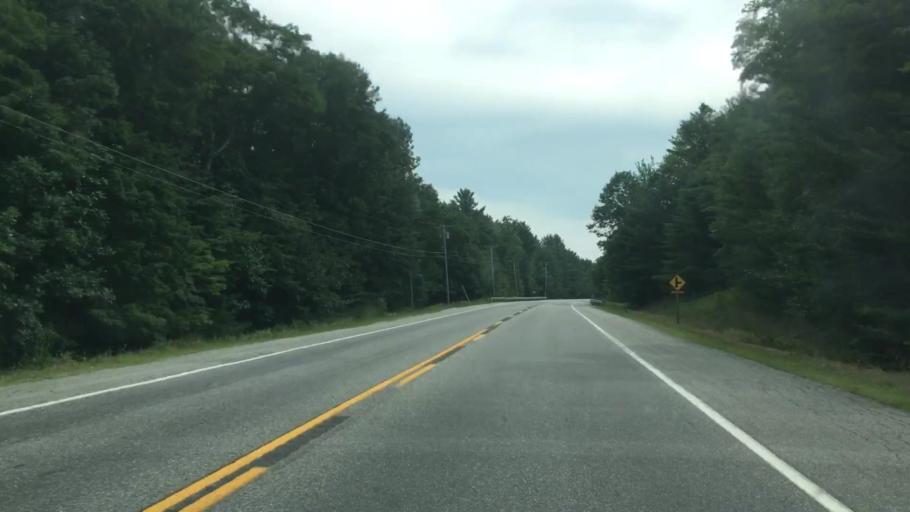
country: US
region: Maine
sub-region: Oxford County
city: Bethel
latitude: 44.4849
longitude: -70.7895
